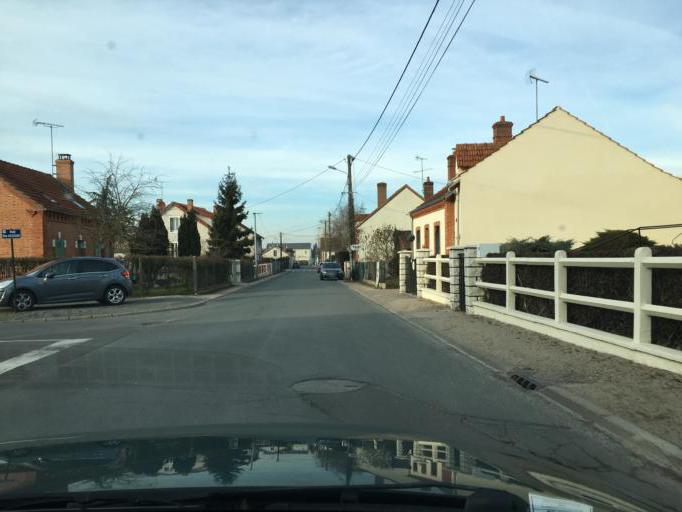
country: FR
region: Centre
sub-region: Departement du Loiret
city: La Ferte-Saint-Aubin
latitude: 47.7146
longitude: 1.9397
